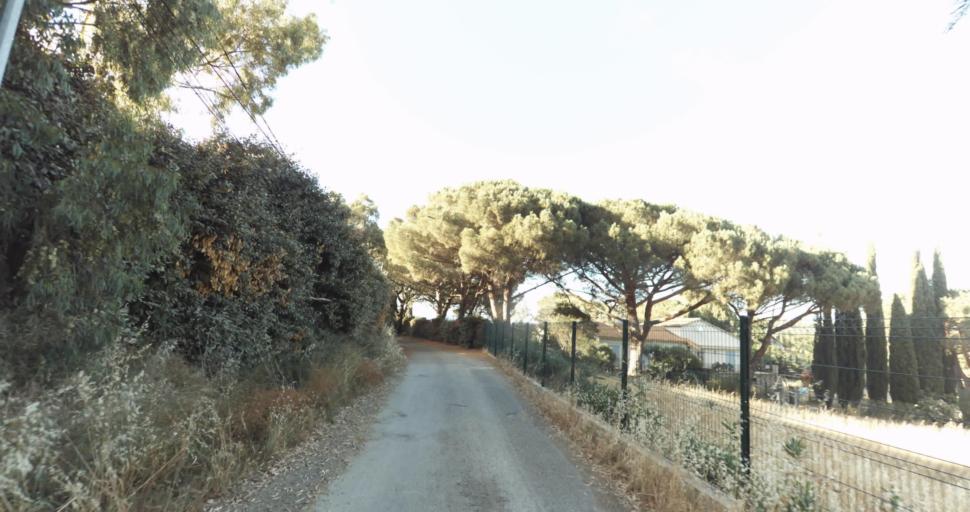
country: FR
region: Provence-Alpes-Cote d'Azur
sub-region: Departement du Var
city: La Croix-Valmer
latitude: 43.2155
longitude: 6.5646
